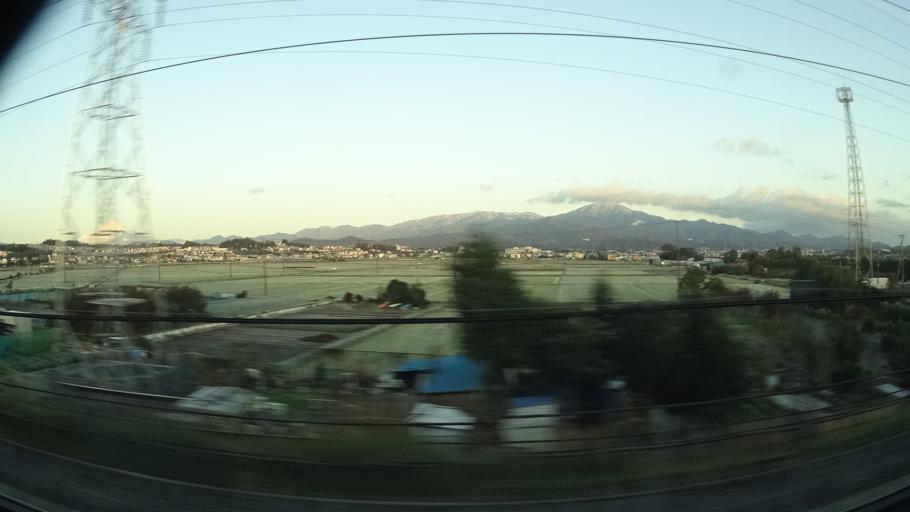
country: JP
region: Kanagawa
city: Hiratsuka
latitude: 35.3485
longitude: 139.3134
